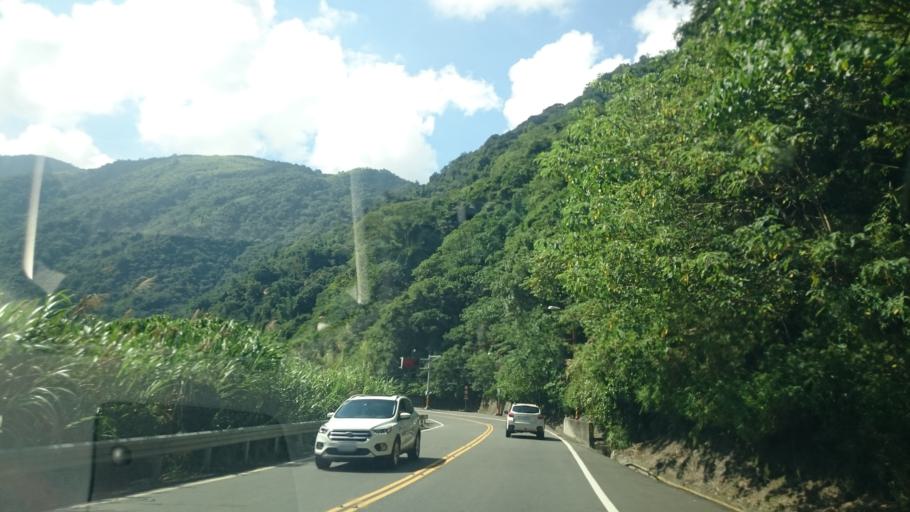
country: TW
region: Taiwan
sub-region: Nantou
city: Puli
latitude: 24.0003
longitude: 121.0667
